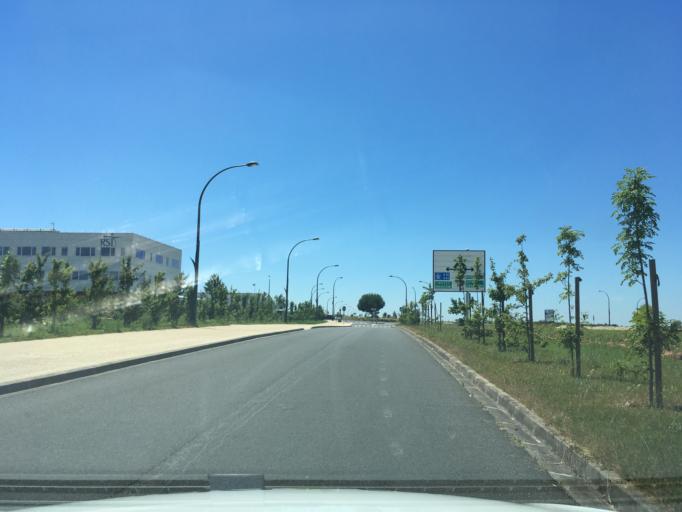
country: FR
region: Poitou-Charentes
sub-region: Departement des Deux-Sevres
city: Aiffres
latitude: 46.3190
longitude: -0.4128
